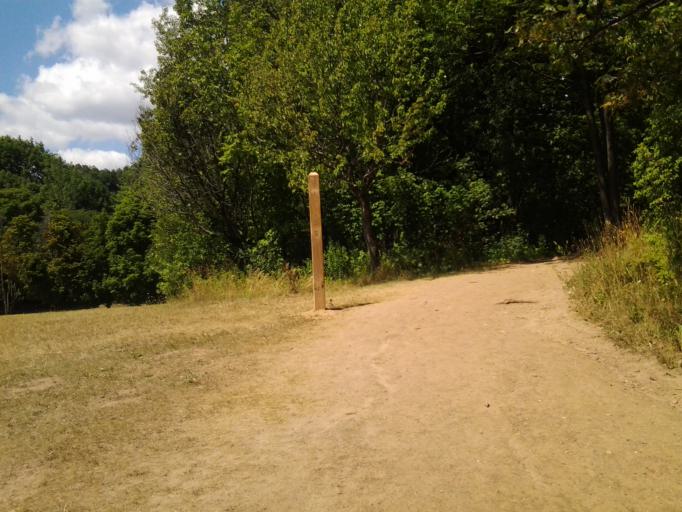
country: CA
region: Ontario
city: Ancaster
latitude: 43.2764
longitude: -79.9793
